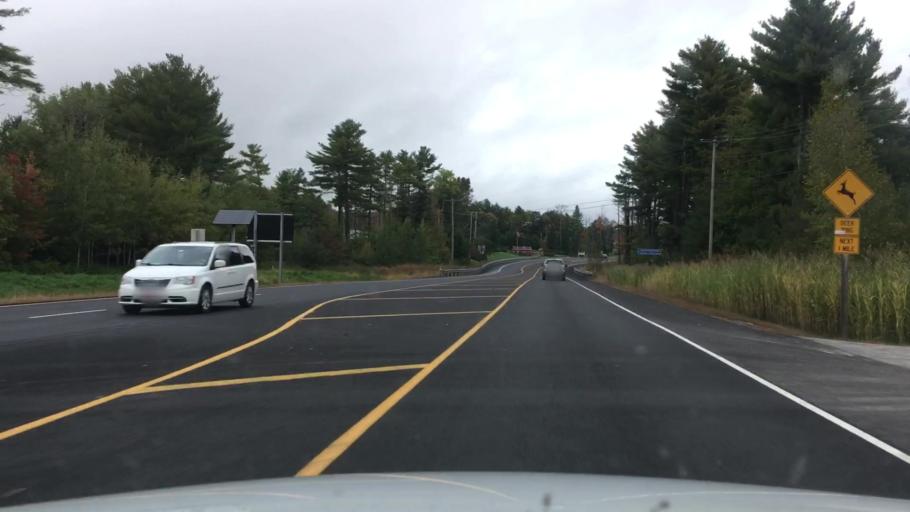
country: US
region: Maine
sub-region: Cumberland County
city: New Gloucester
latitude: 43.8841
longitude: -70.3394
